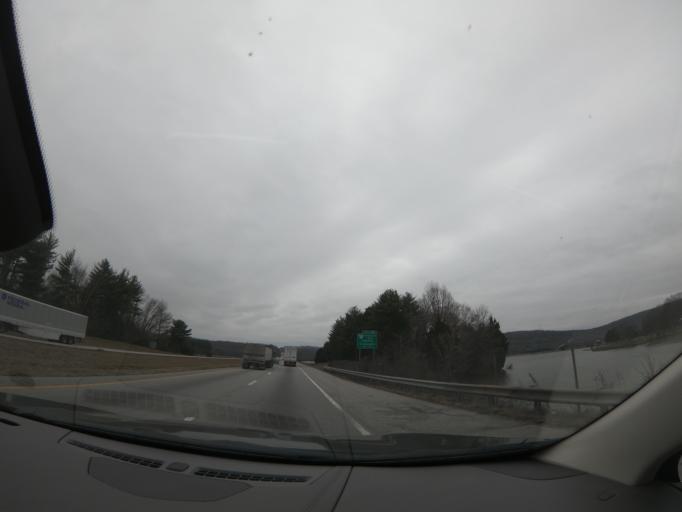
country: US
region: Tennessee
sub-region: Marion County
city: Jasper
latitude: 35.0271
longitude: -85.5637
